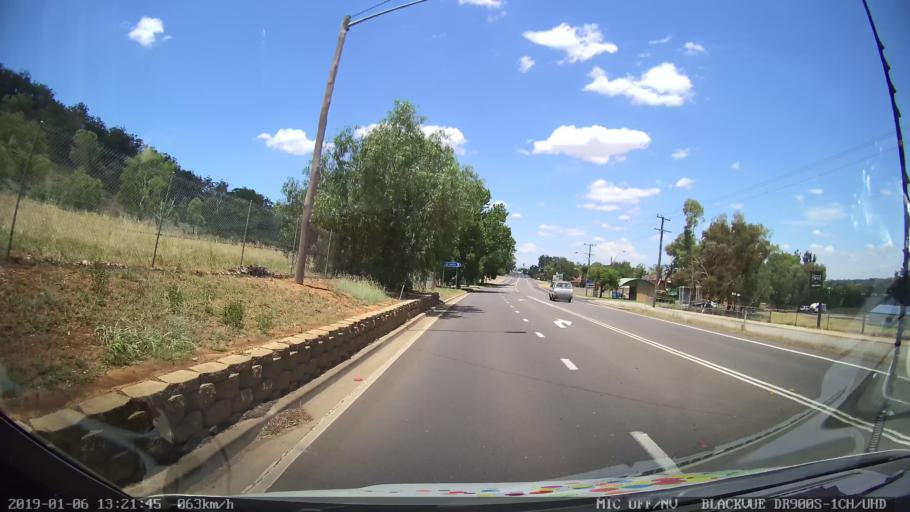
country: AU
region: New South Wales
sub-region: Tamworth Municipality
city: East Tamworth
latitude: -31.1075
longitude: 150.9536
